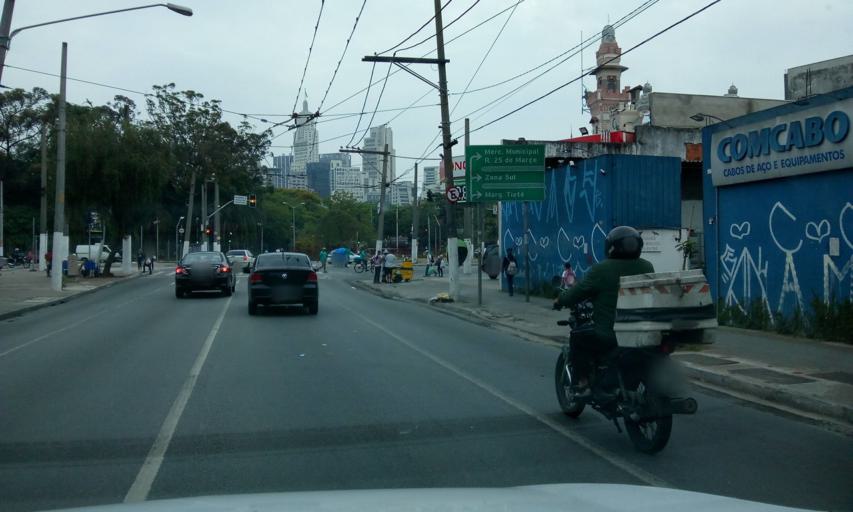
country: BR
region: Sao Paulo
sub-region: Sao Paulo
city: Sao Paulo
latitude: -23.5447
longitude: -46.6257
